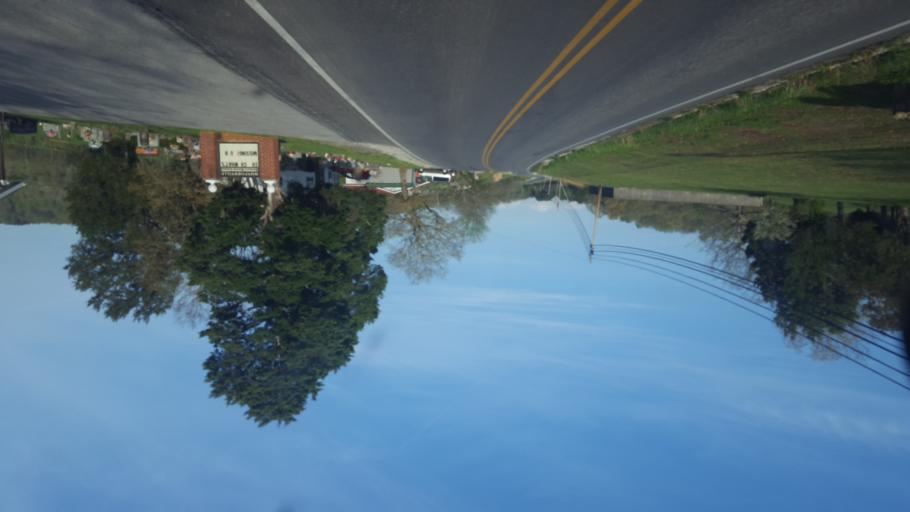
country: US
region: Kentucky
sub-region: Hart County
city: Munfordville
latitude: 37.2754
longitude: -85.9167
